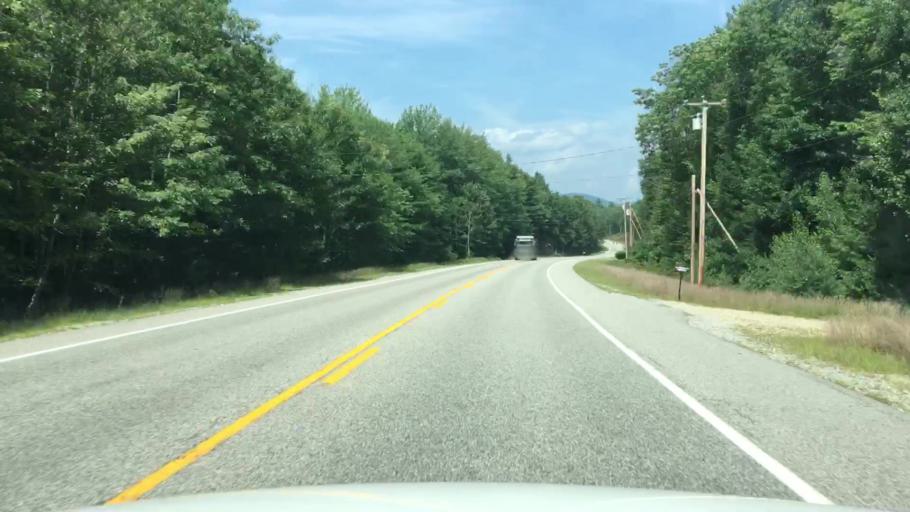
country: US
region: Maine
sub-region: Oxford County
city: Canton
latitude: 44.4734
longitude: -70.3264
